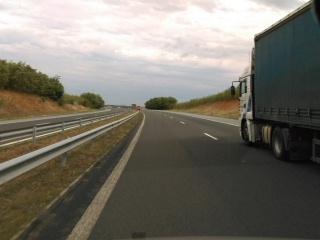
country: BG
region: Yambol
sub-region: Obshtina Yambol
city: Yambol
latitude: 42.5398
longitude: 26.4700
